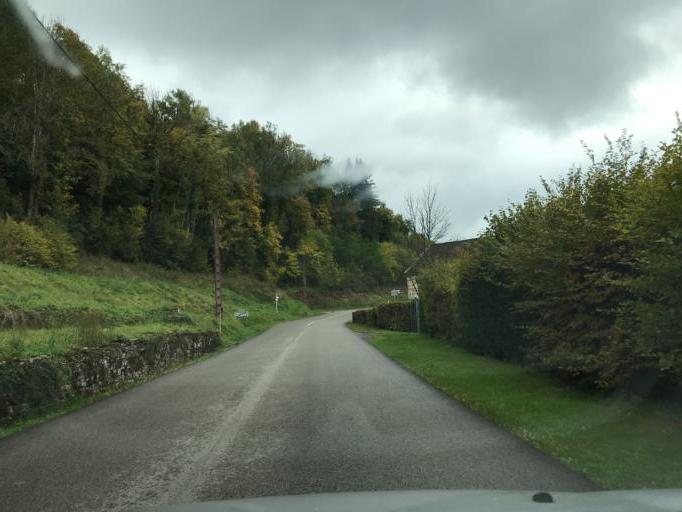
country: FR
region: Rhone-Alpes
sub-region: Departement de l'Ain
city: Coligny
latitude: 46.3988
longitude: 5.4529
